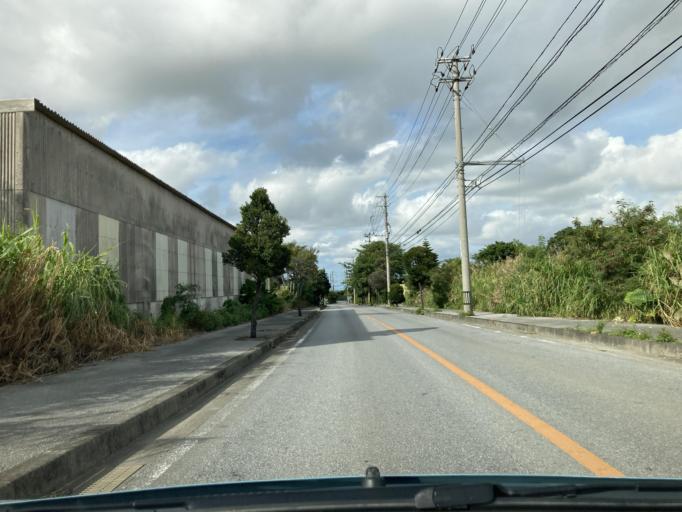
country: JP
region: Okinawa
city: Itoman
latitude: 26.1249
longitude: 127.7136
